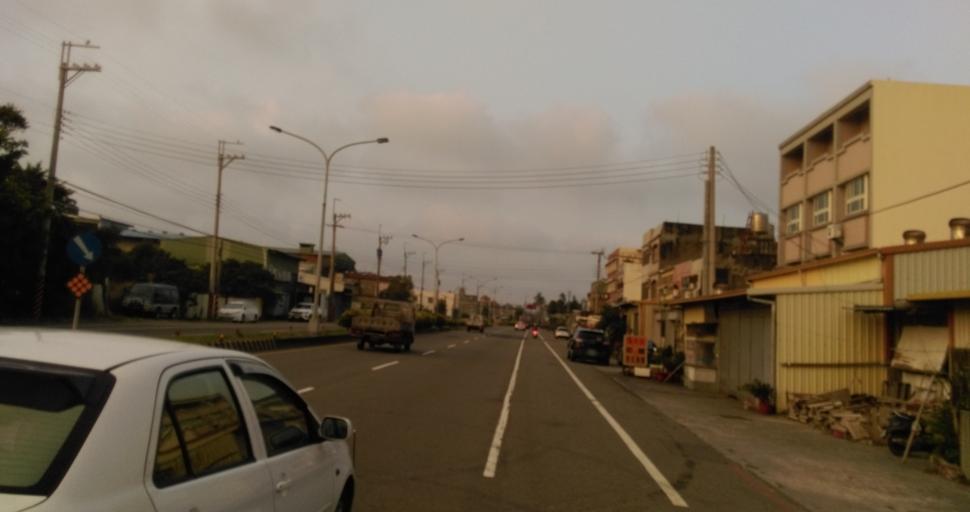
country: TW
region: Taiwan
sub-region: Hsinchu
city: Hsinchu
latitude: 24.8156
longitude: 120.9231
